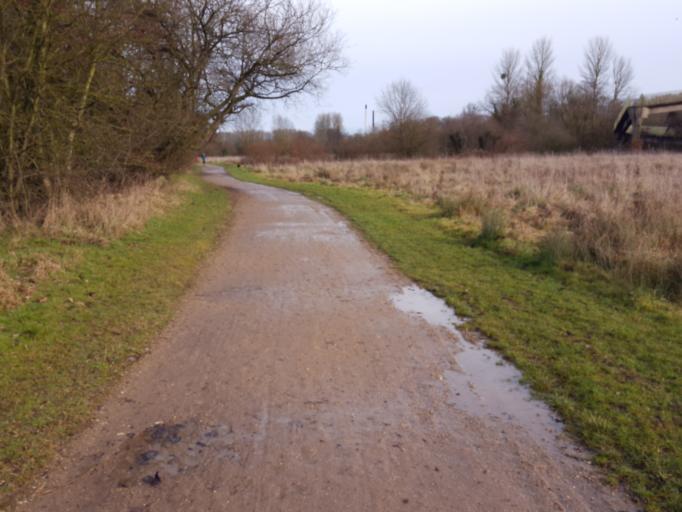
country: GB
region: England
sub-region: Essex
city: Harlow
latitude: 51.7831
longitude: 0.0992
